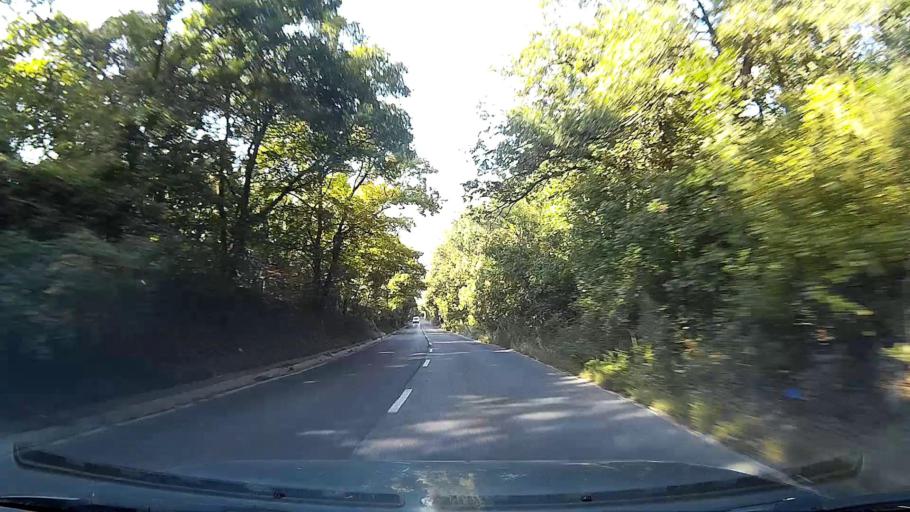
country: HU
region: Pest
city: Diosd
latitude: 47.4301
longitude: 18.9804
